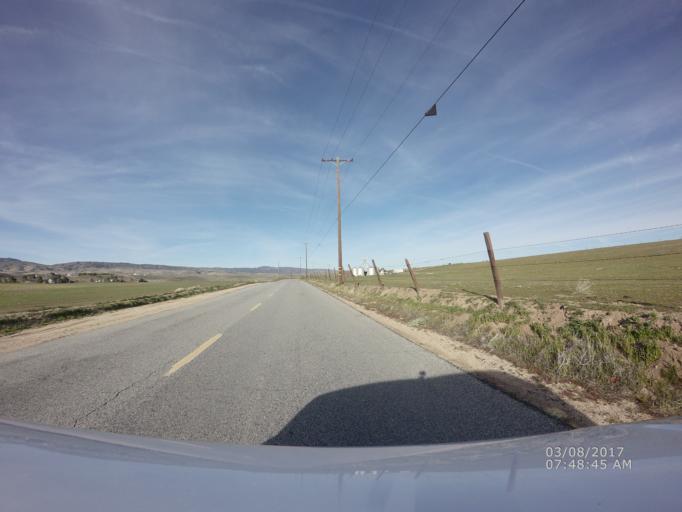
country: US
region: California
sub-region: Los Angeles County
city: Green Valley
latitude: 34.7135
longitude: -118.3522
